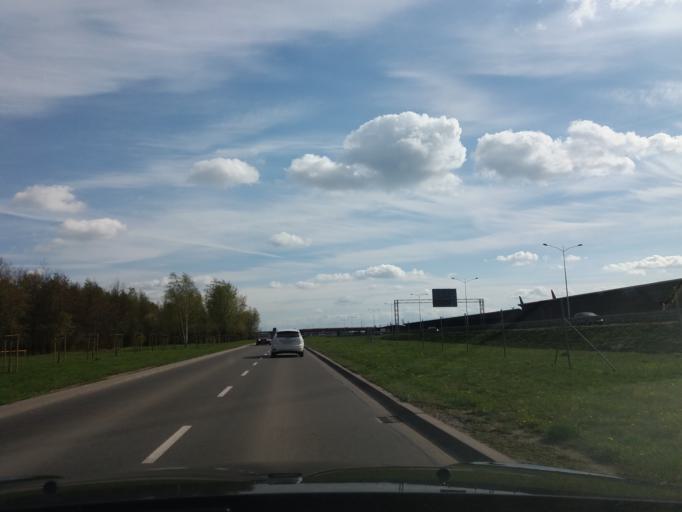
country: PL
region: Lower Silesian Voivodeship
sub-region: Powiat wroclawski
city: Smolec
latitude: 51.1138
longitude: 16.9336
